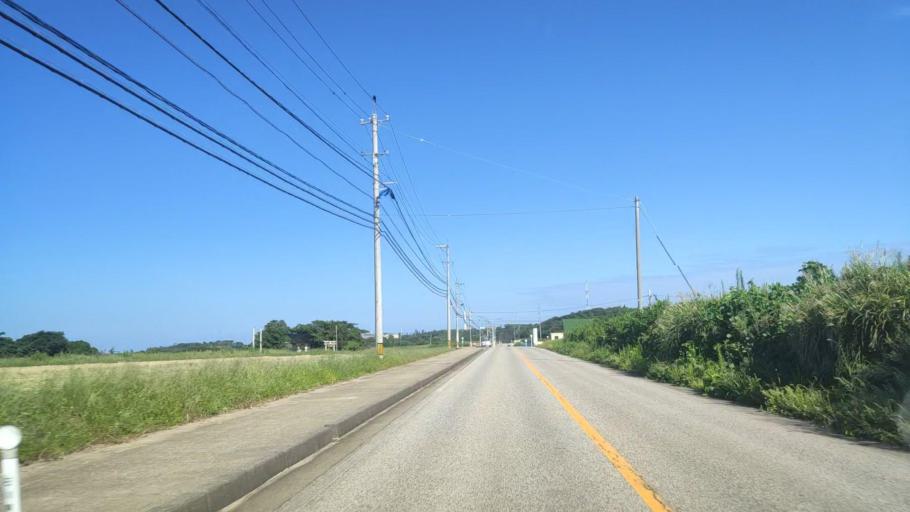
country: JP
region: Ishikawa
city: Hakui
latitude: 37.0445
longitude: 136.7391
